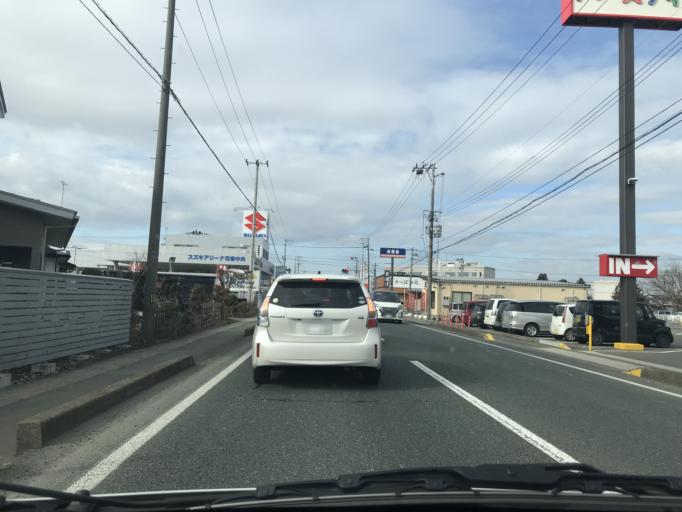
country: JP
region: Iwate
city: Hanamaki
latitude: 39.3896
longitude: 141.1245
